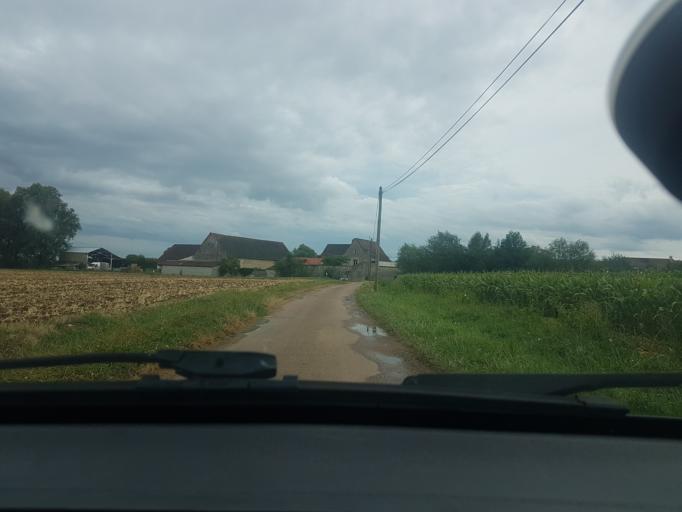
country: FR
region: Bourgogne
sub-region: Departement de Saone-et-Loire
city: Rully
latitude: 46.8773
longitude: 4.7563
